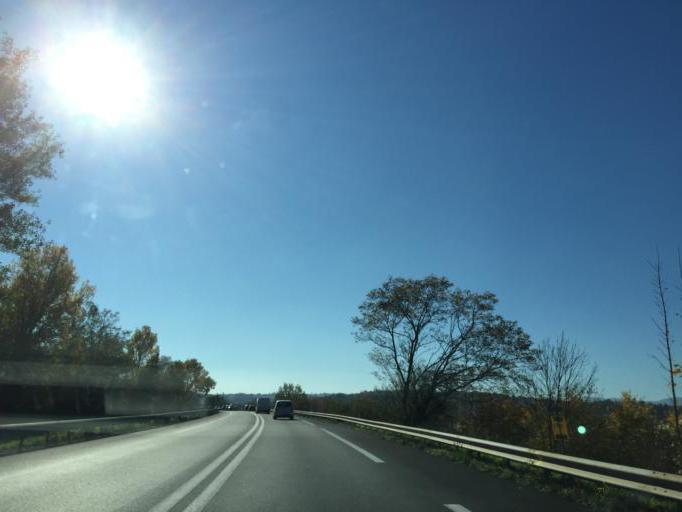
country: FR
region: Rhone-Alpes
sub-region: Departement du Rhone
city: Brignais
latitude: 45.6679
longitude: 4.7635
